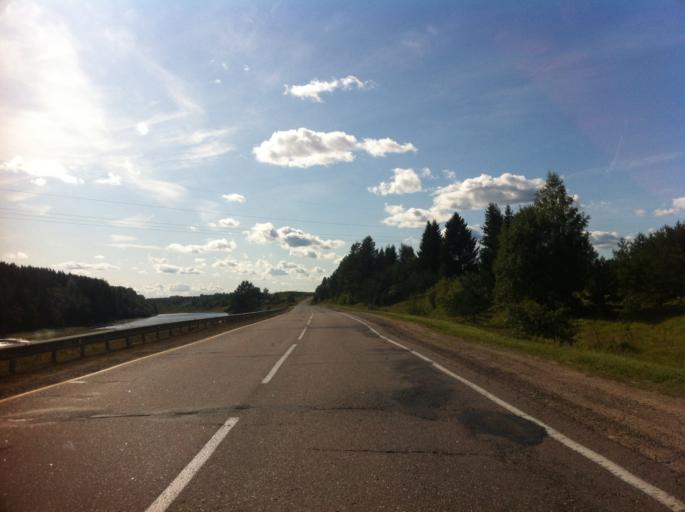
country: RU
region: Pskov
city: Izborsk
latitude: 57.7496
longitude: 27.7479
